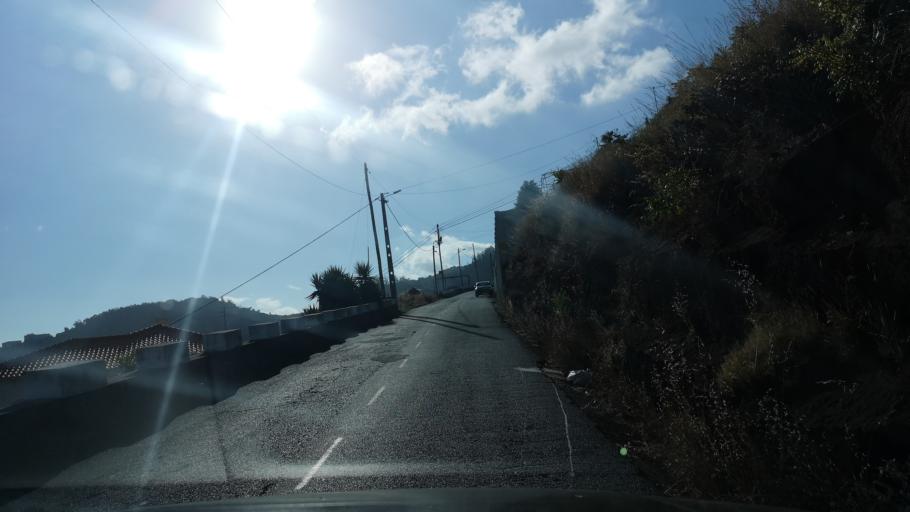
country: PT
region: Madeira
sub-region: Santa Cruz
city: Camacha
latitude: 32.6573
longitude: -16.8361
